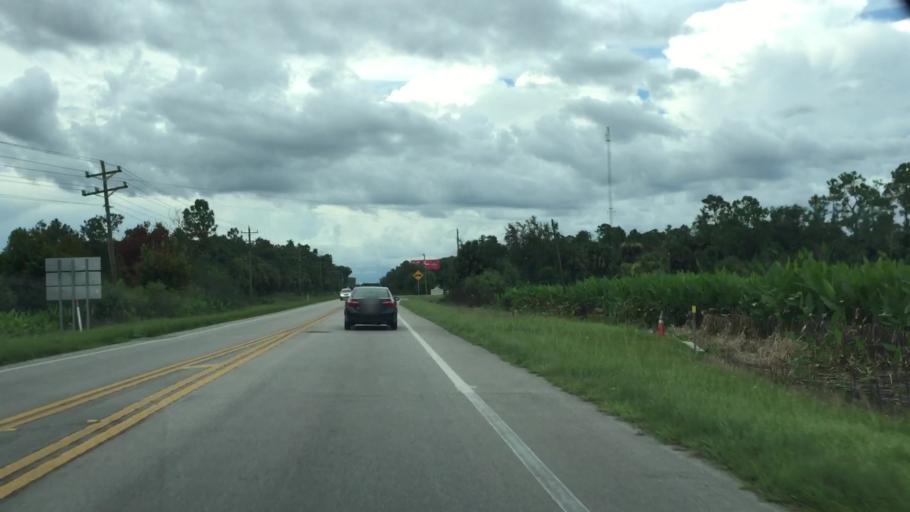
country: US
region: Florida
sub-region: Collier County
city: Immokalee
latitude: 26.3982
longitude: -81.4171
